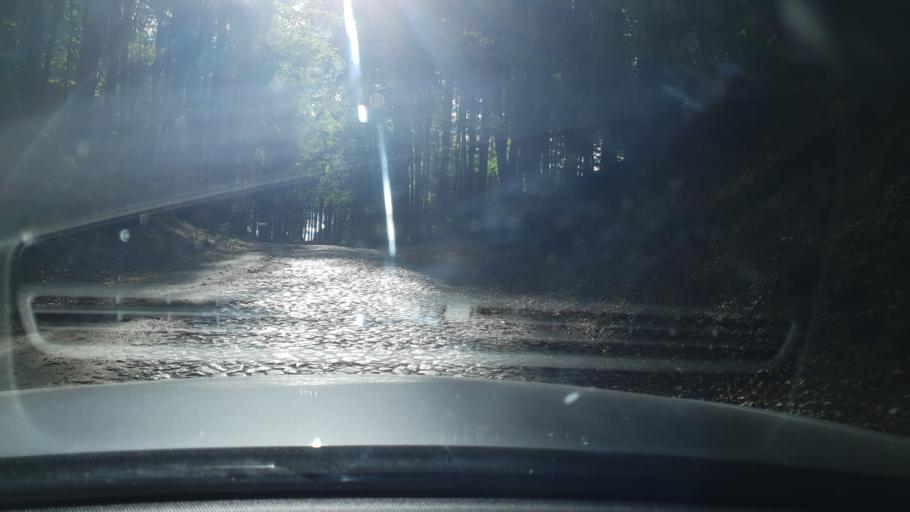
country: PL
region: Pomeranian Voivodeship
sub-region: Powiat wejherowski
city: Reda
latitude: 54.5845
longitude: 18.3161
